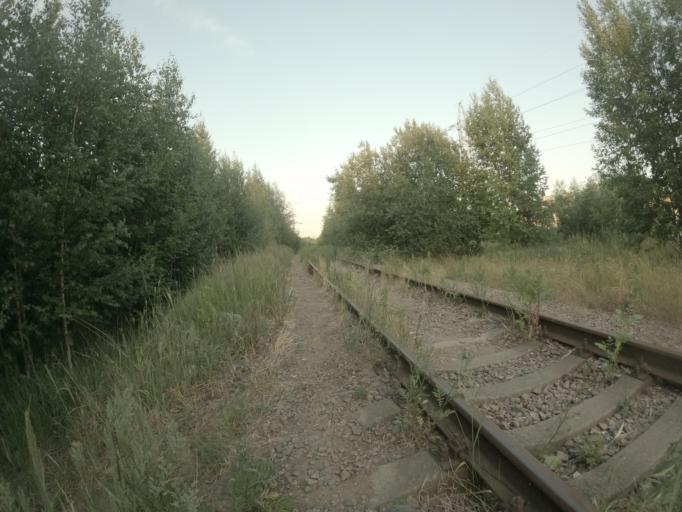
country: RU
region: St.-Petersburg
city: Krasnogvargeisky
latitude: 59.9399
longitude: 30.4443
